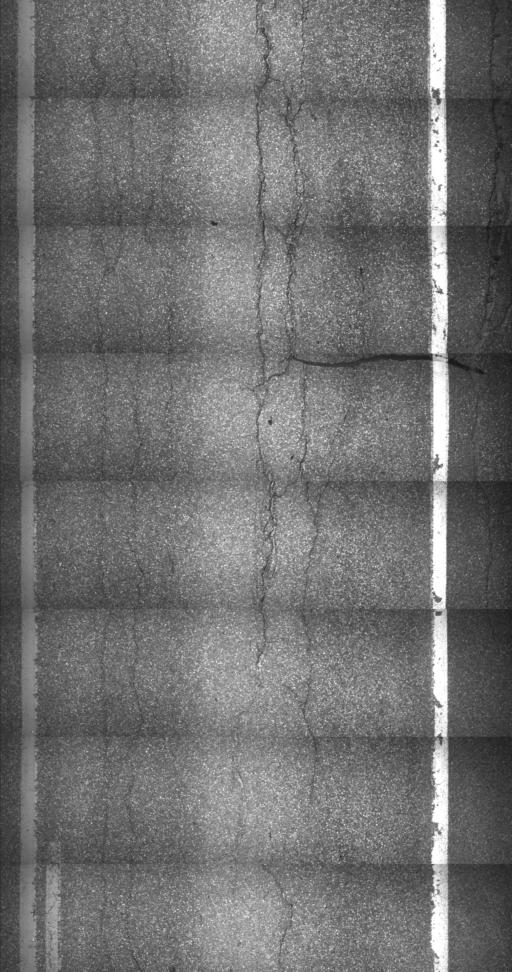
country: US
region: Vermont
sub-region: Addison County
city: Bristol
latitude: 44.1055
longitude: -73.0968
